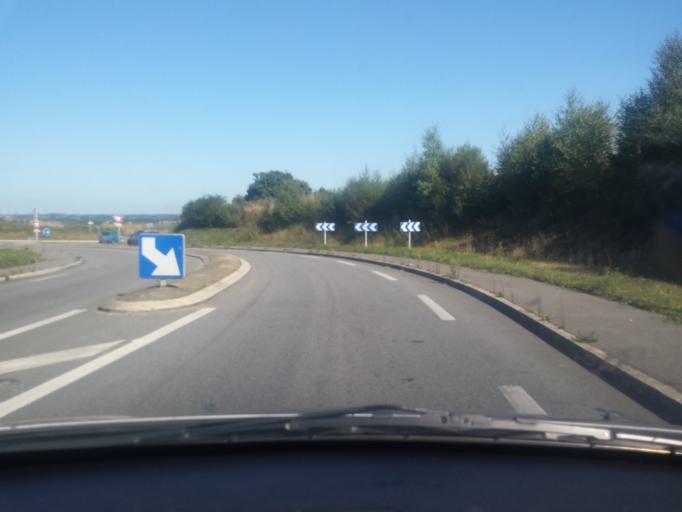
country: FR
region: Brittany
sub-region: Departement du Morbihan
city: Malguenac
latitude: 48.0978
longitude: -3.0238
